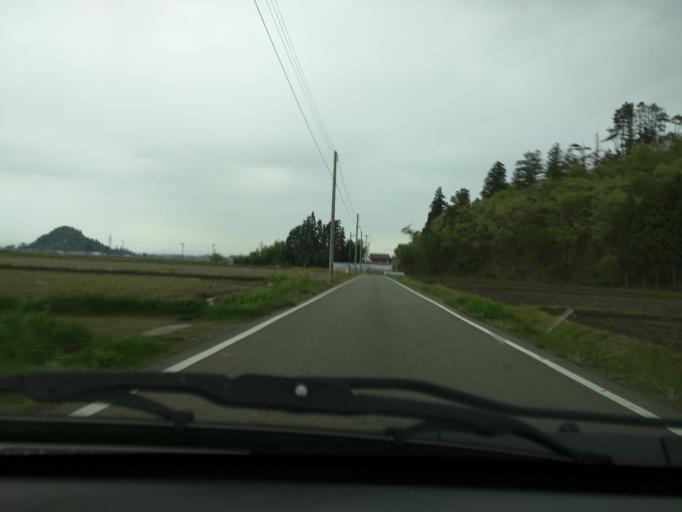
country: JP
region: Fukushima
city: Kitakata
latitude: 37.4314
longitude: 139.8879
